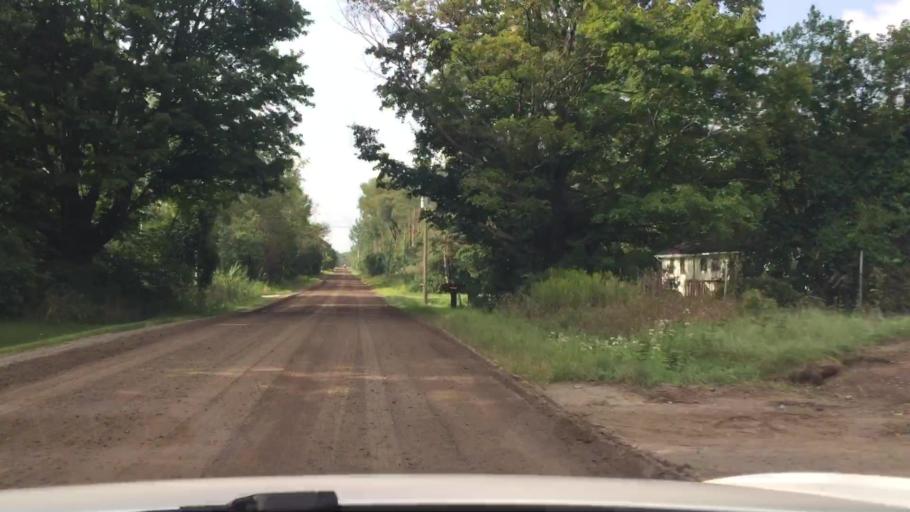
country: CA
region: Ontario
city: Oshawa
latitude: 43.9306
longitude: -78.7430
